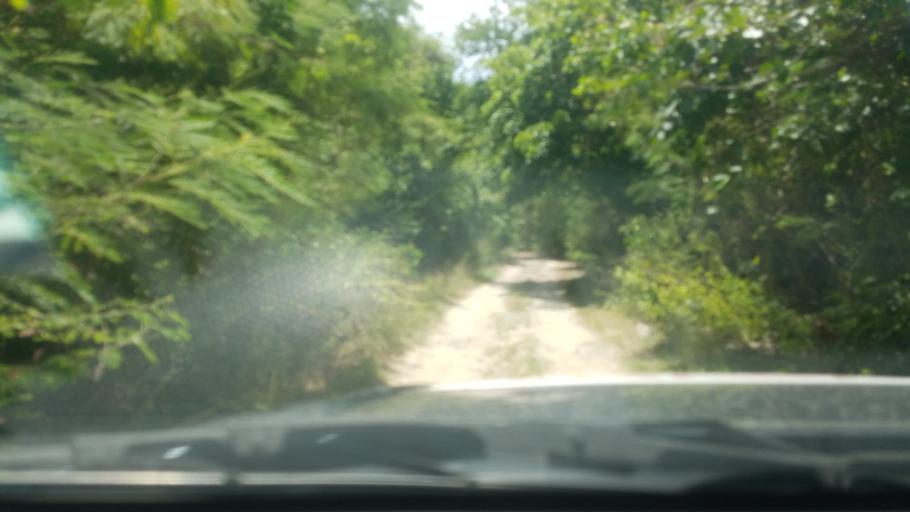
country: LC
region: Vieux-Fort
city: Vieux Fort
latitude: 13.7514
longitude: -60.9378
